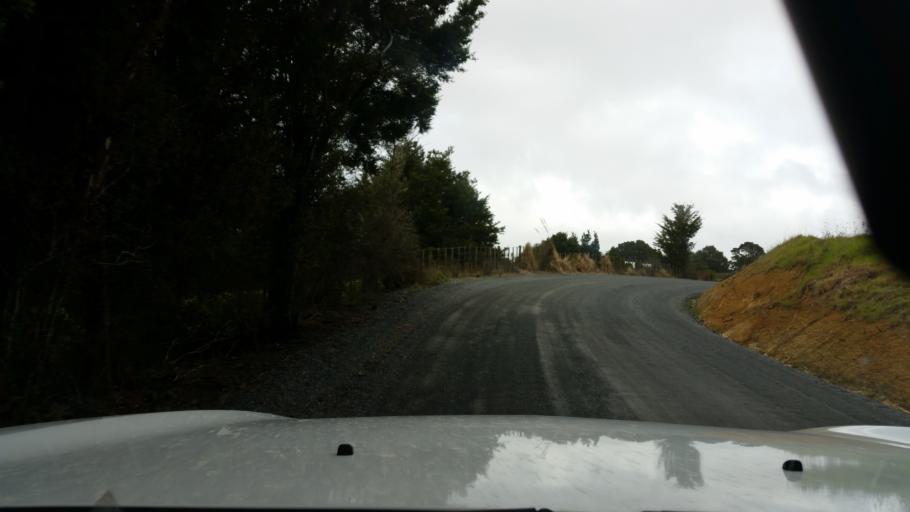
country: NZ
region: Northland
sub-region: Whangarei
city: Whangarei
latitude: -35.7323
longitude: 174.4232
